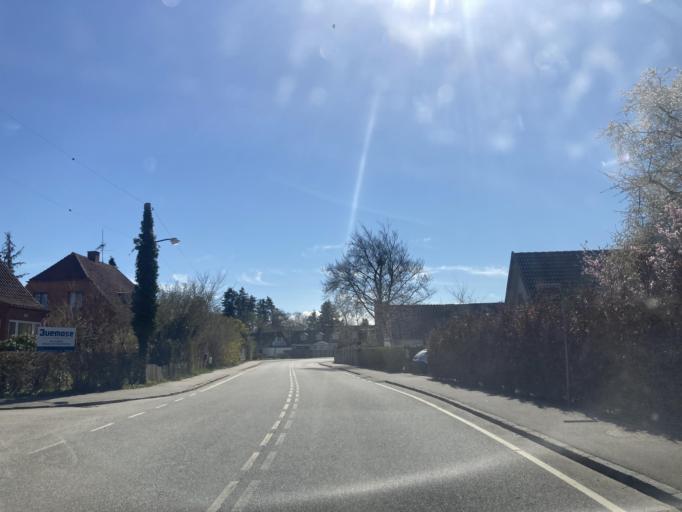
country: DK
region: Capital Region
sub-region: Gribskov Kommune
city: Graested
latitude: 56.0272
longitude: 12.2801
